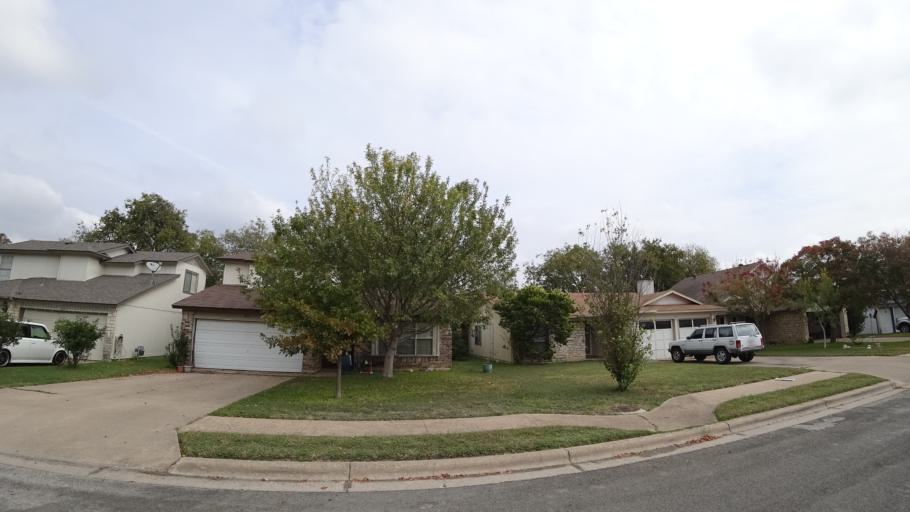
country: US
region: Texas
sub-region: Williamson County
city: Round Rock
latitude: 30.4917
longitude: -97.6905
